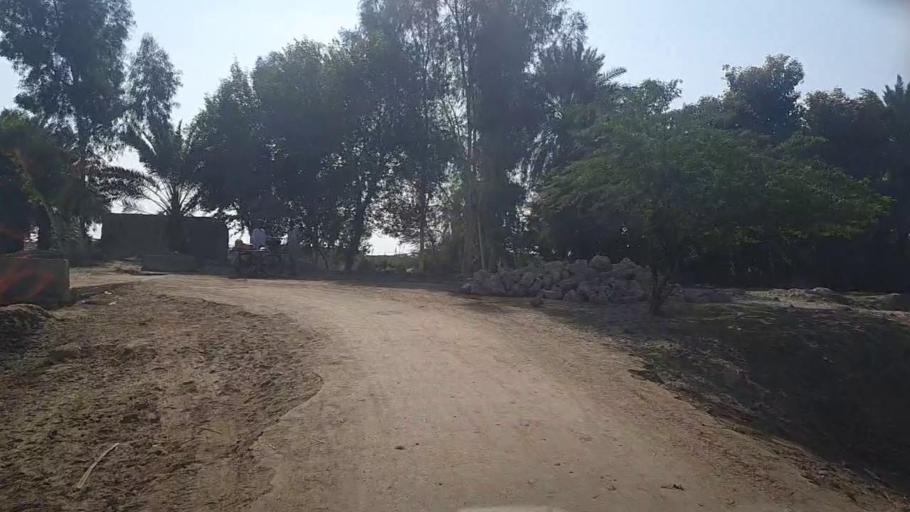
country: PK
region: Sindh
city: Kot Diji
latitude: 27.4222
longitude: 68.7371
